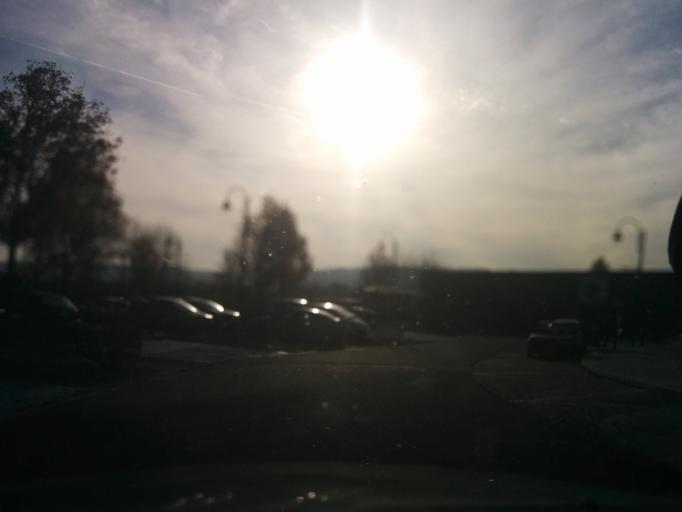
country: FR
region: Haute-Normandie
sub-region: Departement de l'Eure
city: Vernon
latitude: 49.0988
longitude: 1.4587
